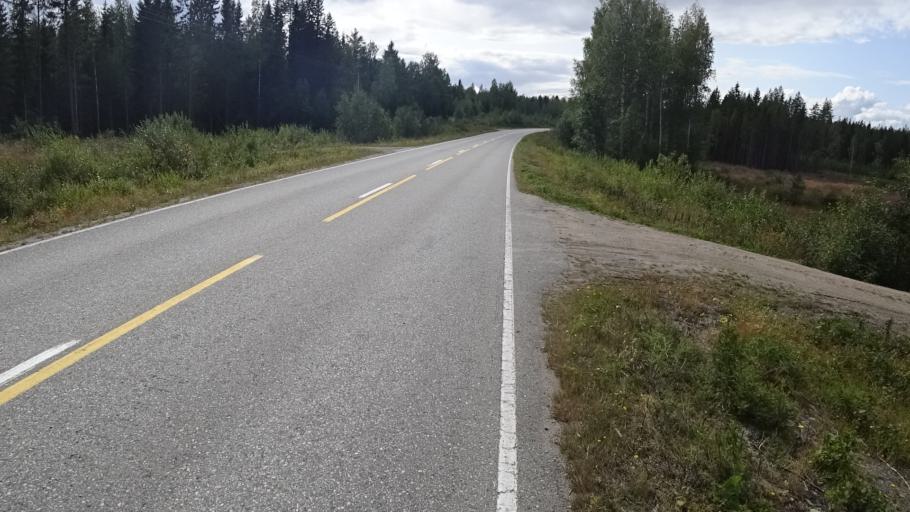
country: FI
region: North Karelia
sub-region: Joensuu
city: Ilomantsi
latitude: 62.6301
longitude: 31.2730
